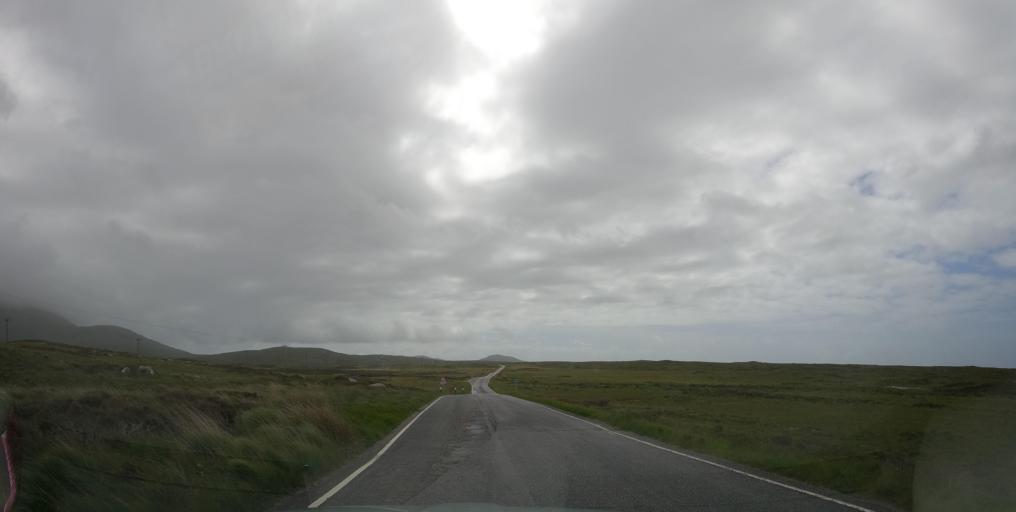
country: GB
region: Scotland
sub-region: Eilean Siar
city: Isle of South Uist
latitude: 57.2822
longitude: -7.3664
